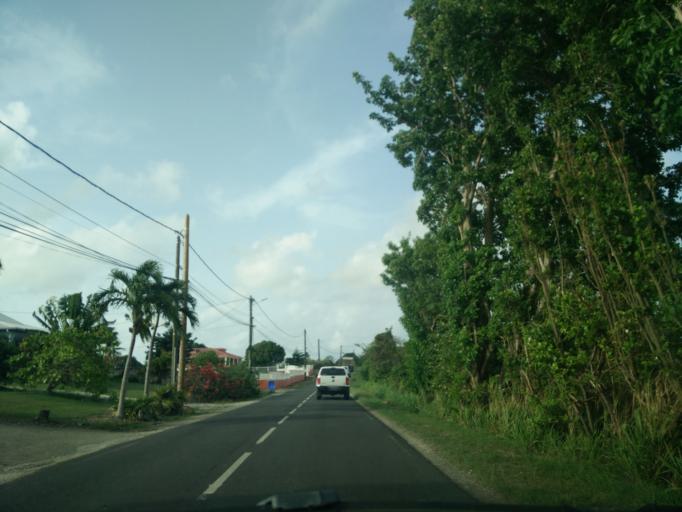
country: GP
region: Guadeloupe
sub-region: Guadeloupe
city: Le Moule
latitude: 16.2890
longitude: -61.3693
